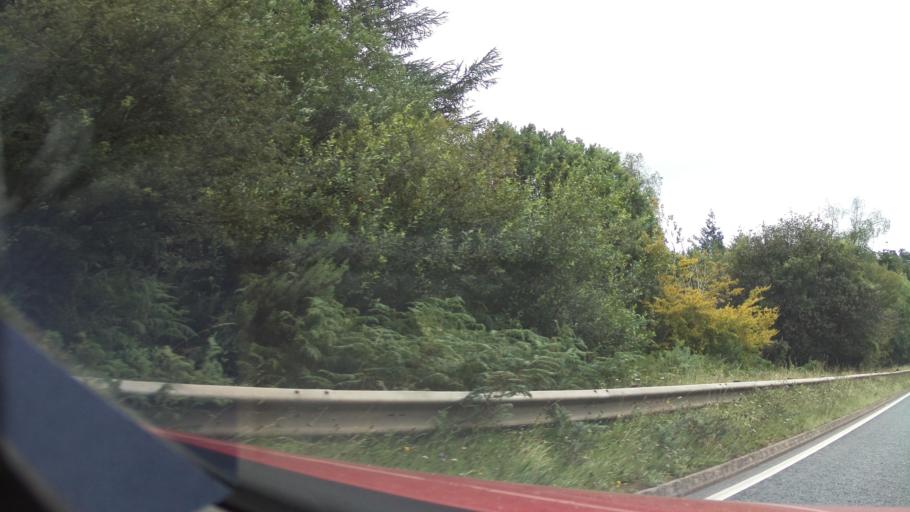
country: GB
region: England
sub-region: Devon
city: Chudleigh
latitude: 50.6313
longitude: -3.5433
